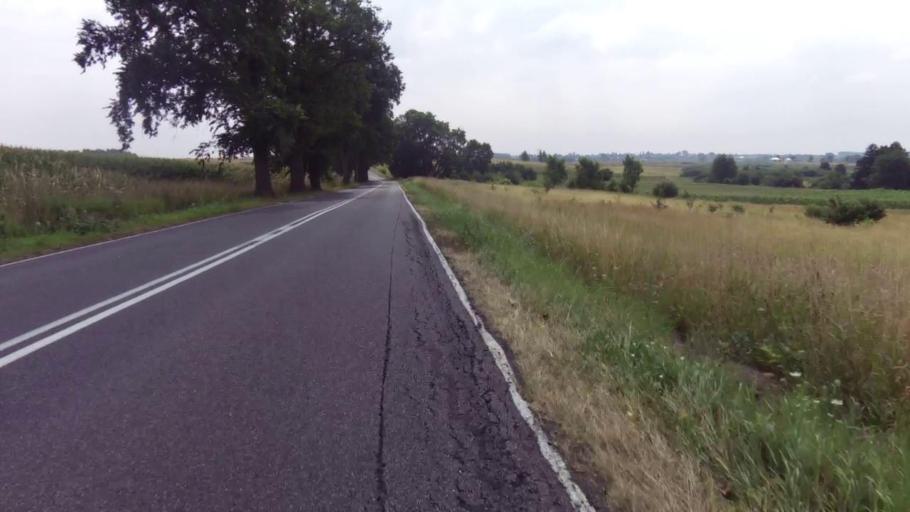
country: PL
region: West Pomeranian Voivodeship
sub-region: Powiat choszczenski
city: Choszczno
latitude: 53.1872
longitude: 15.3973
